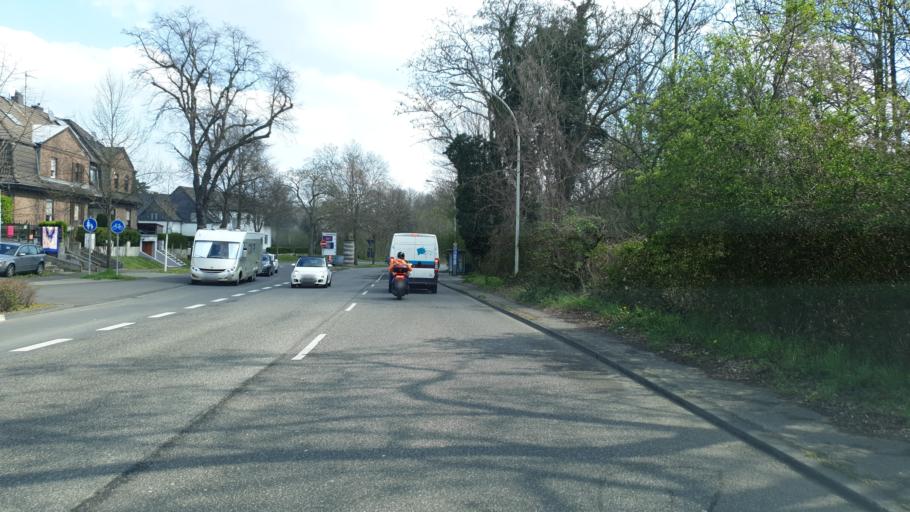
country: DE
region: North Rhine-Westphalia
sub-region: Regierungsbezirk Koln
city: Frechen
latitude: 50.9020
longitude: 6.7898
